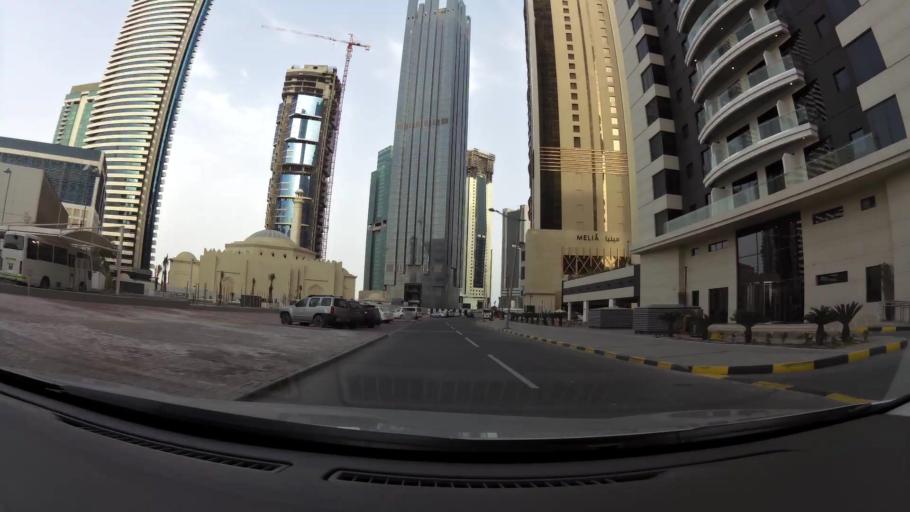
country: QA
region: Baladiyat ad Dawhah
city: Doha
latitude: 25.3293
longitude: 51.5317
